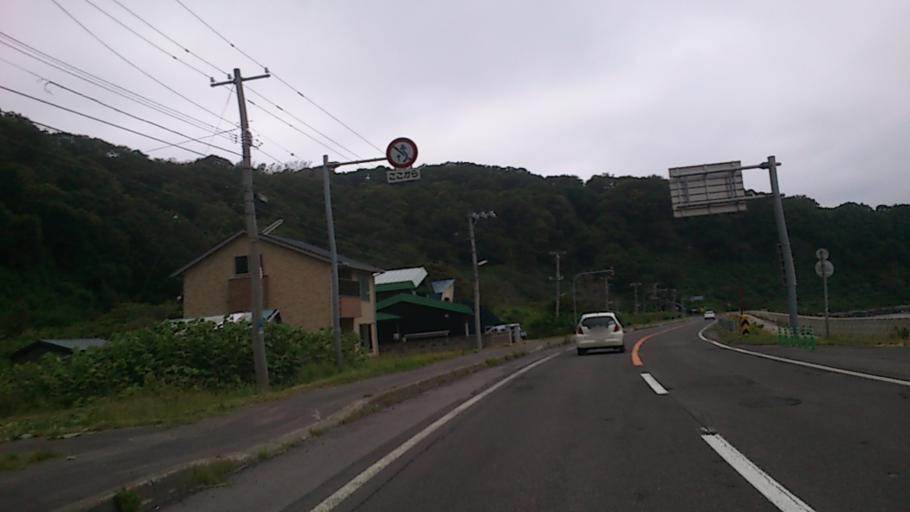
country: JP
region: Hokkaido
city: Iwanai
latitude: 42.6873
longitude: 140.0286
